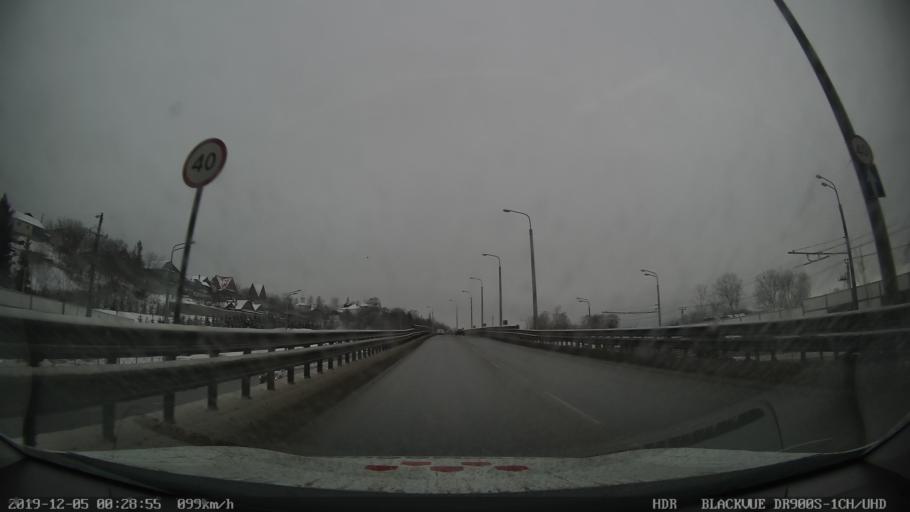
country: RU
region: Tatarstan
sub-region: Gorod Kazan'
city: Kazan
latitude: 55.7487
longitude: 49.1616
